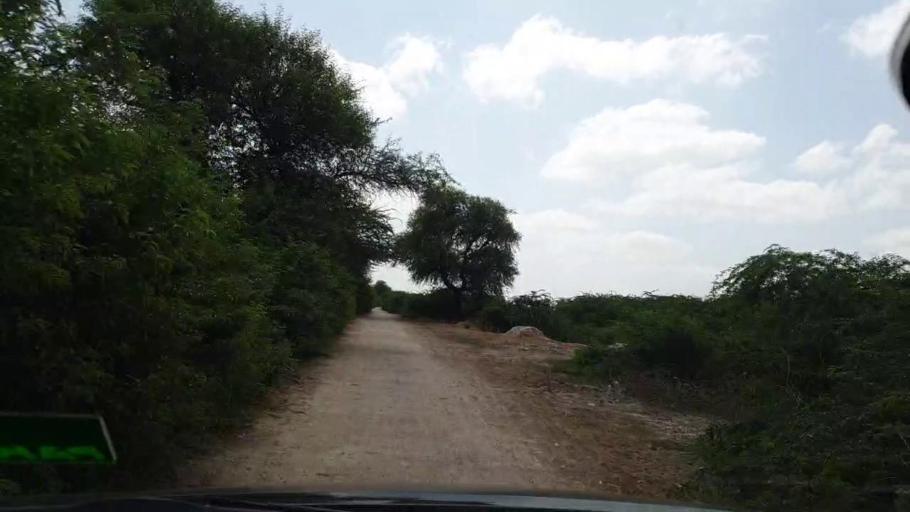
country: PK
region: Sindh
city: Kadhan
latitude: 24.5617
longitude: 69.2112
